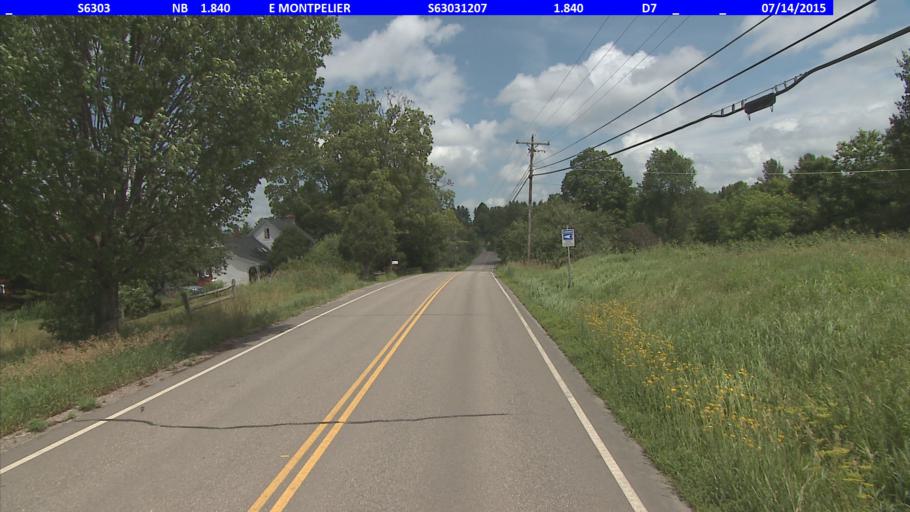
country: US
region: Vermont
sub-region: Washington County
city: Montpelier
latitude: 44.2953
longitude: -72.5382
